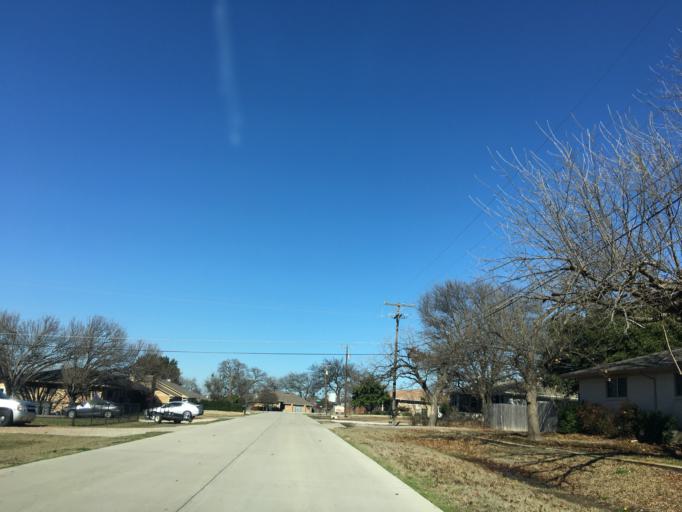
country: US
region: Texas
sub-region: Collin County
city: Prosper
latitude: 33.2390
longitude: -96.7971
